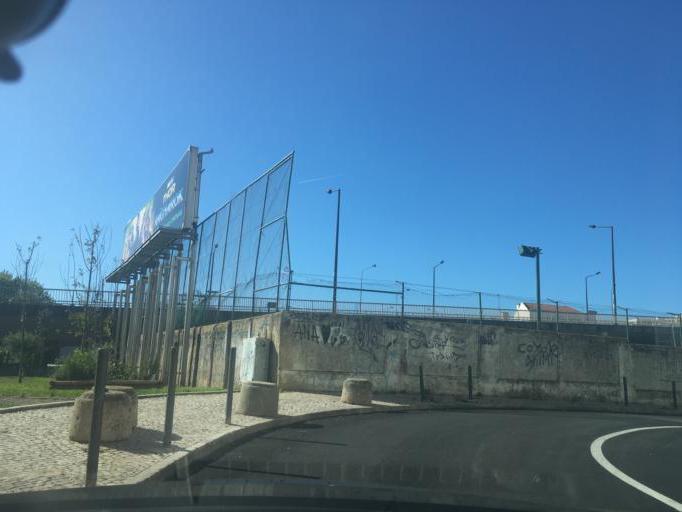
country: PT
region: Lisbon
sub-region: Lisbon
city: Lisbon
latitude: 38.7408
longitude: -9.1581
